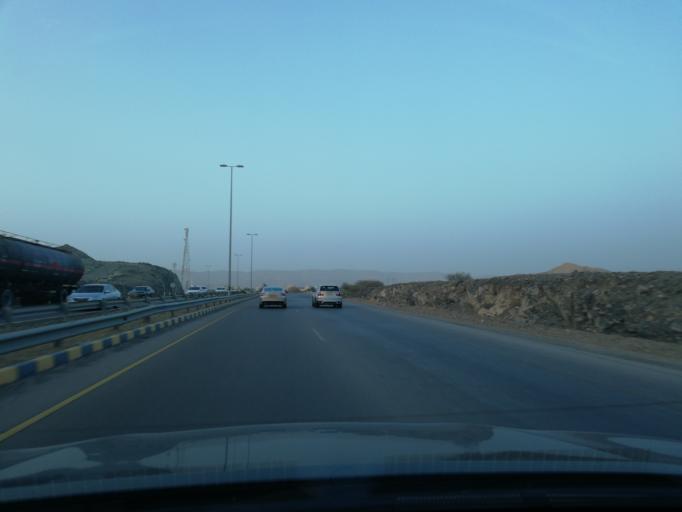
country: OM
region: Muhafazat ad Dakhiliyah
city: Bidbid
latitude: 23.4785
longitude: 58.1972
